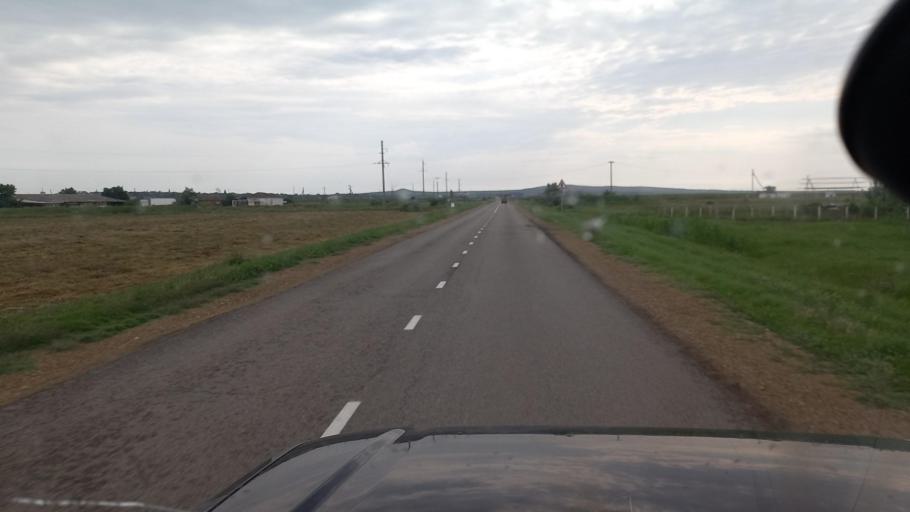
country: RU
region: Krasnodarskiy
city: Akhtanizovskaya
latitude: 45.3437
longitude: 37.1228
